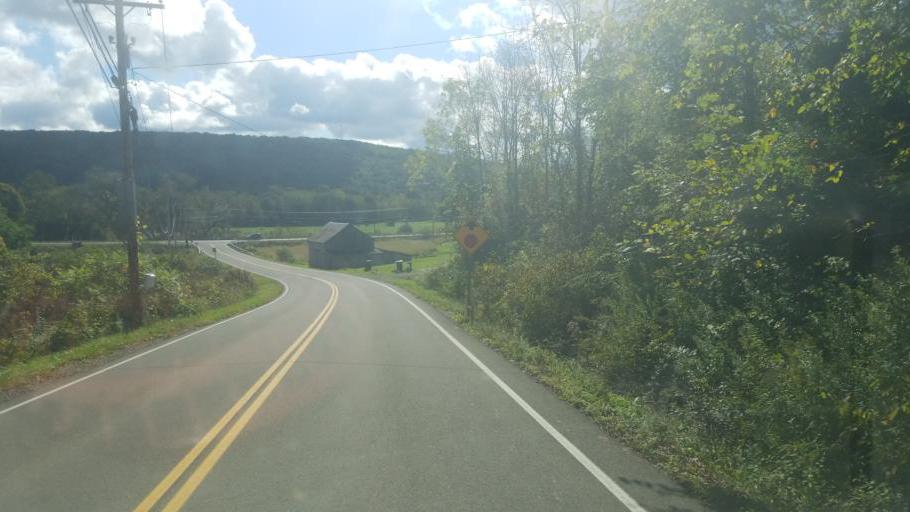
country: US
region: New York
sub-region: Allegany County
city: Cuba
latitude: 42.2426
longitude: -78.2752
